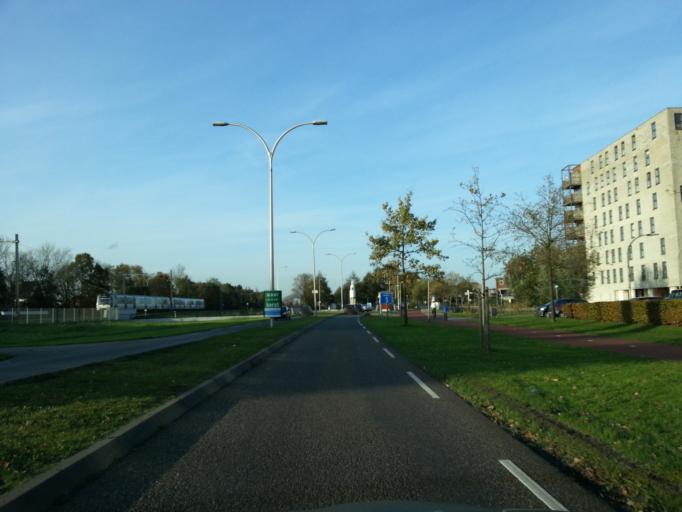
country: NL
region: South Holland
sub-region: Gemeente Pijnacker-Nootdorp
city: Pijnacker
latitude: 52.0079
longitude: 4.4456
